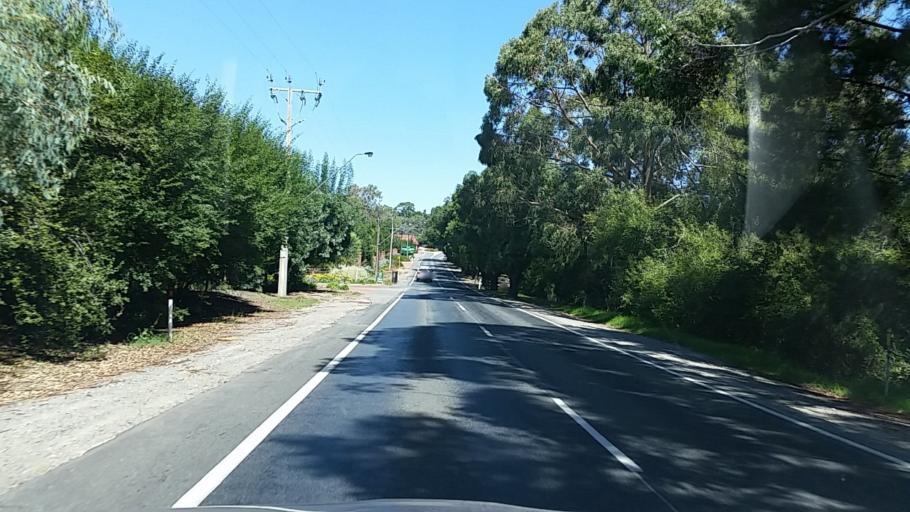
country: AU
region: South Australia
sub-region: Mount Barker
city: Little Hampton
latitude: -35.0459
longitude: 138.8643
